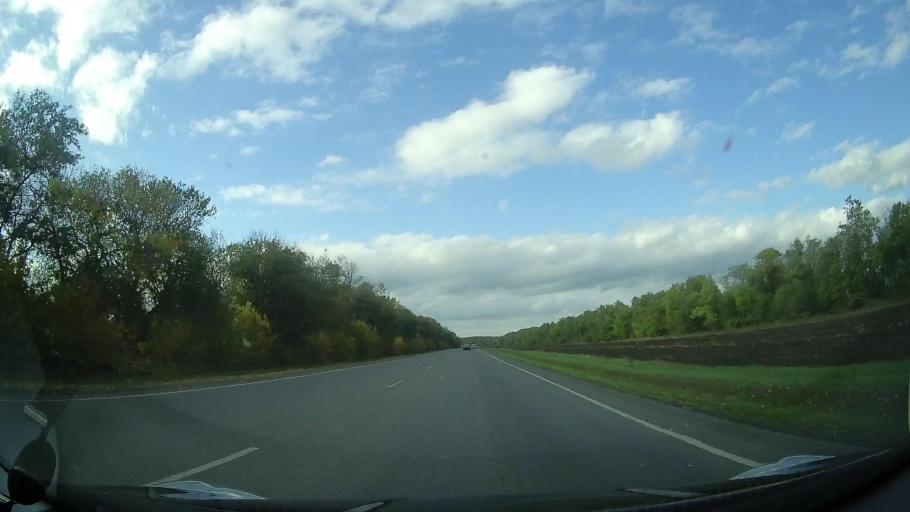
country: RU
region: Rostov
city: Kirovskaya
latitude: 46.9532
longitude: 40.0795
